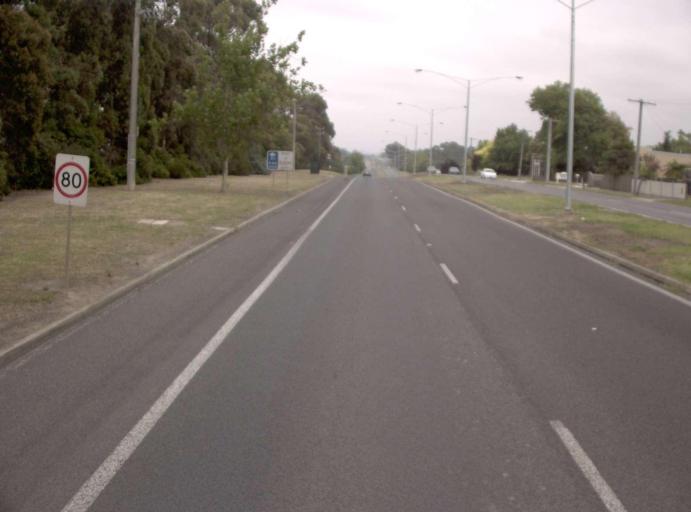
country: AU
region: Victoria
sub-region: Latrobe
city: Traralgon
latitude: -38.2033
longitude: 146.5189
